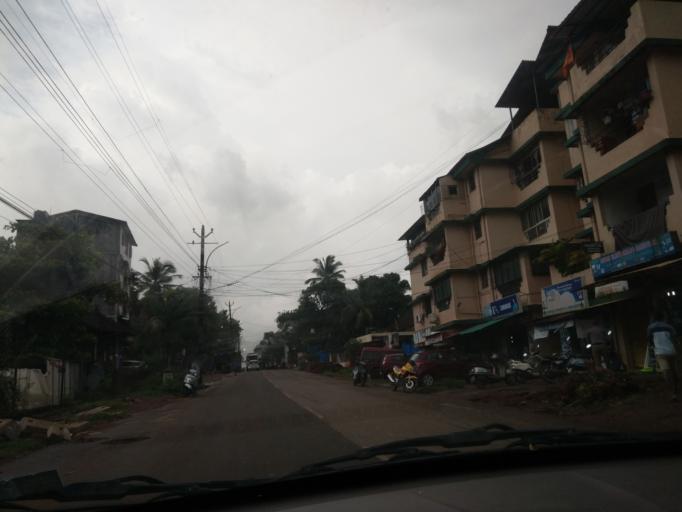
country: IN
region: Goa
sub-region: South Goa
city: Raia
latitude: 15.2934
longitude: 73.9666
